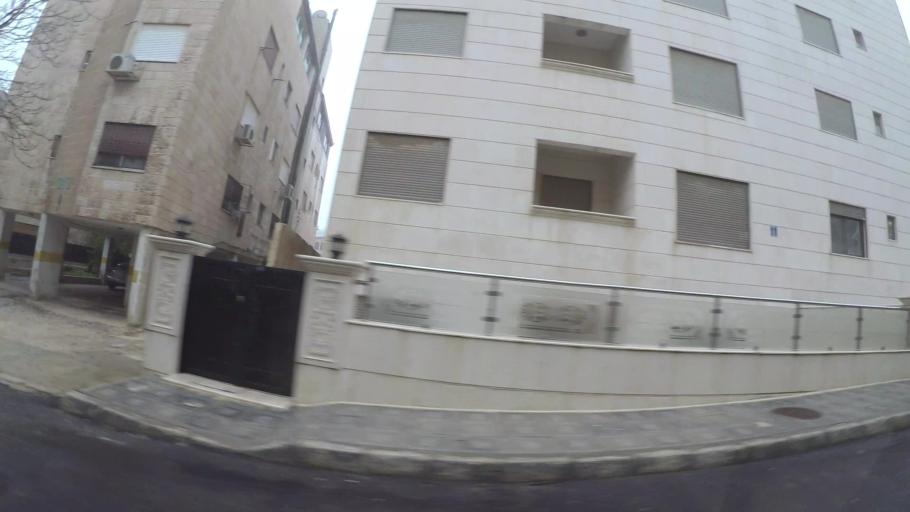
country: JO
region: Amman
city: Wadi as Sir
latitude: 31.9629
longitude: 35.8770
